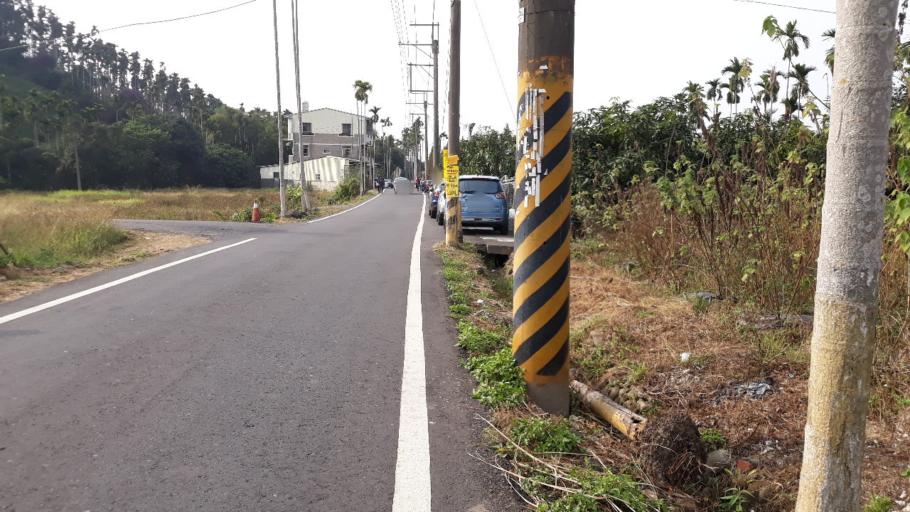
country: TW
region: Taiwan
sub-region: Chiayi
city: Jiayi Shi
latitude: 23.4304
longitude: 120.5198
